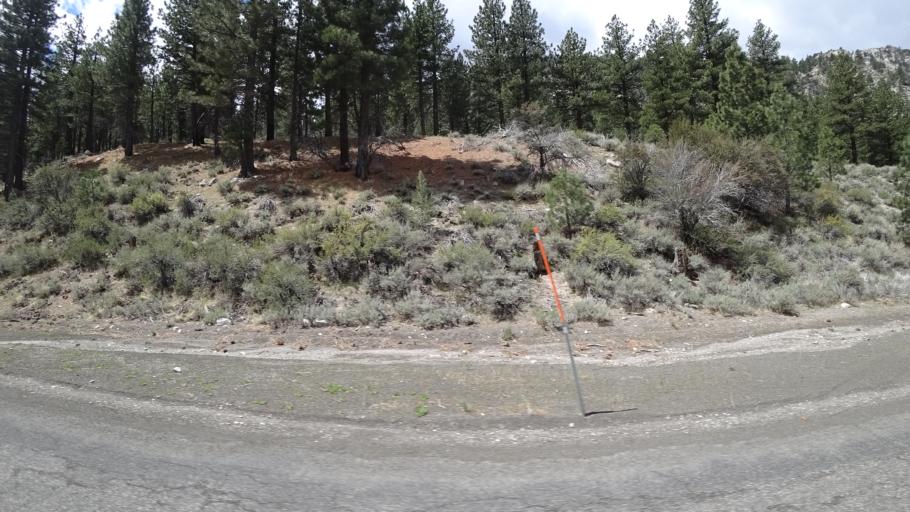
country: US
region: California
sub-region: Mono County
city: Bridgeport
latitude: 38.4452
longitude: -119.4549
